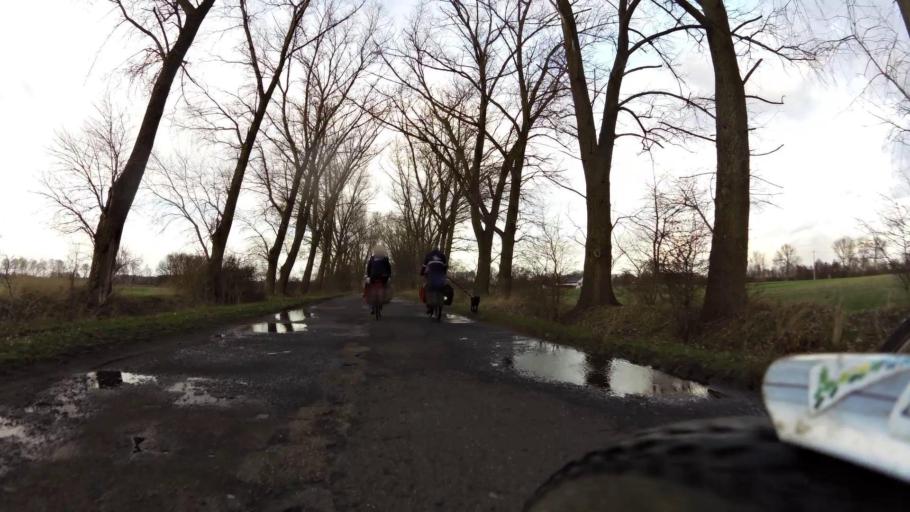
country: PL
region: West Pomeranian Voivodeship
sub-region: Powiat kamienski
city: Kamien Pomorski
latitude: 53.9149
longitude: 14.7319
